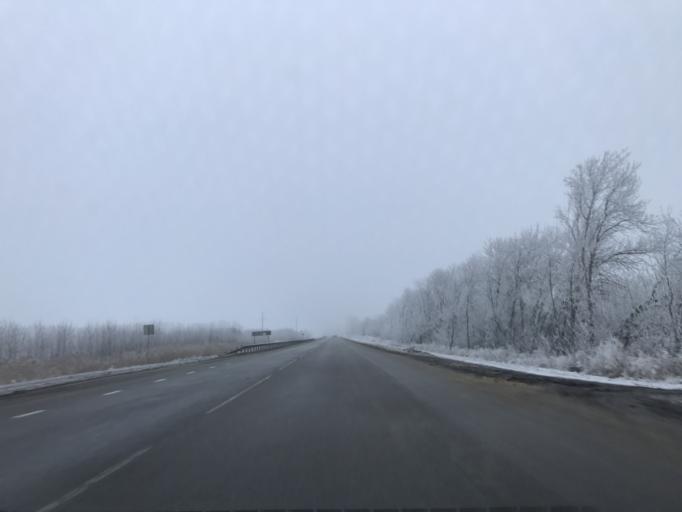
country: RU
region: Rostov
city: Grushevskaya
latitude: 47.3787
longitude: 39.8820
